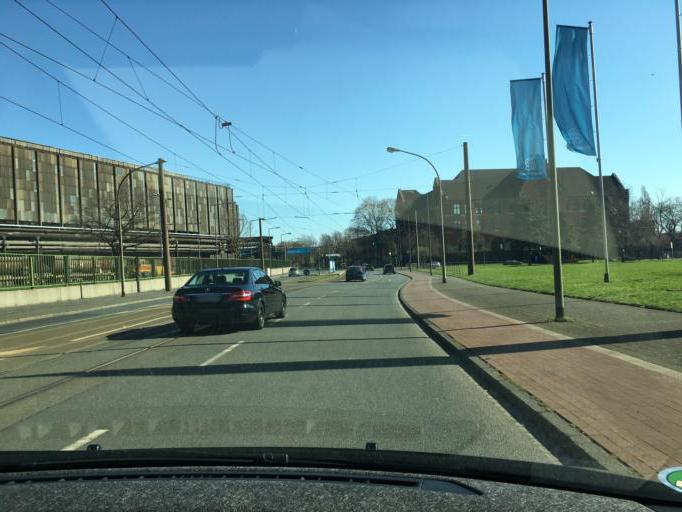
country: DE
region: North Rhine-Westphalia
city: Meiderich
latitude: 51.4917
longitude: 6.7421
